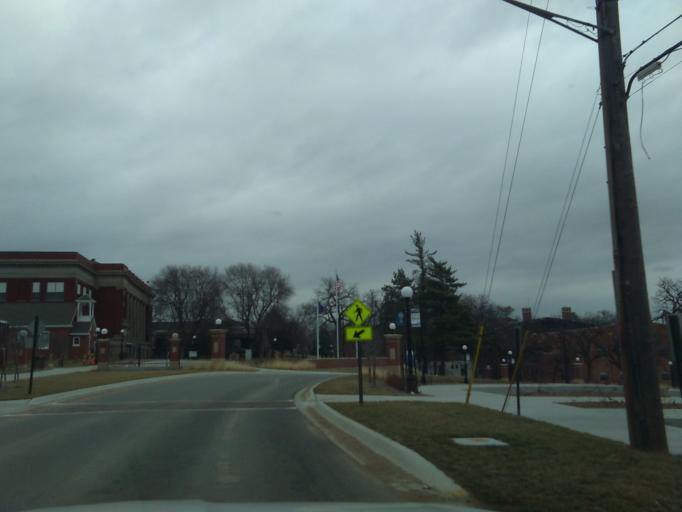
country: US
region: Nebraska
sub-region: Nemaha County
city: Auburn
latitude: 40.4732
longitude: -95.7337
